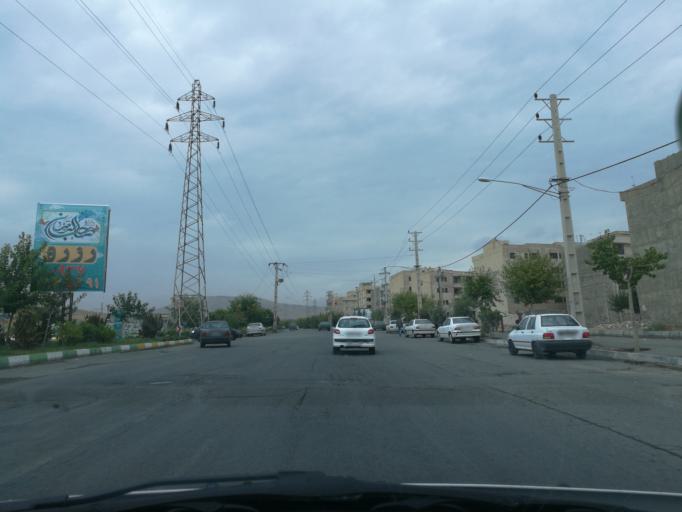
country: IR
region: Alborz
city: Karaj
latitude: 35.8620
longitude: 50.9257
